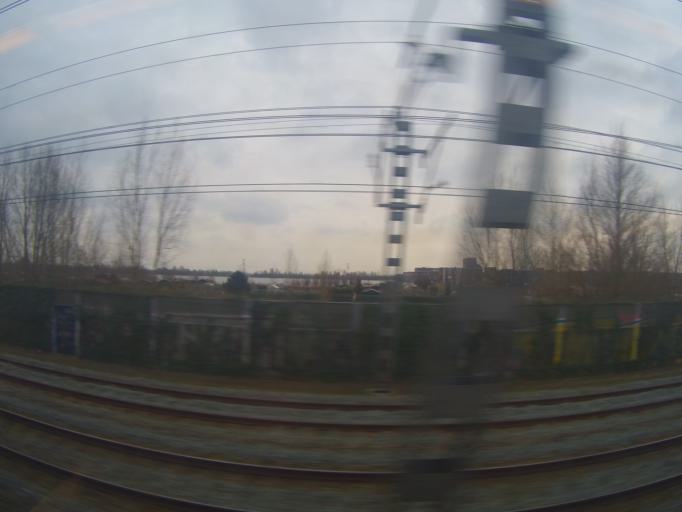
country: NL
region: Utrecht
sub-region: Gemeente Woerden
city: Woerden
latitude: 52.0925
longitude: 4.9157
